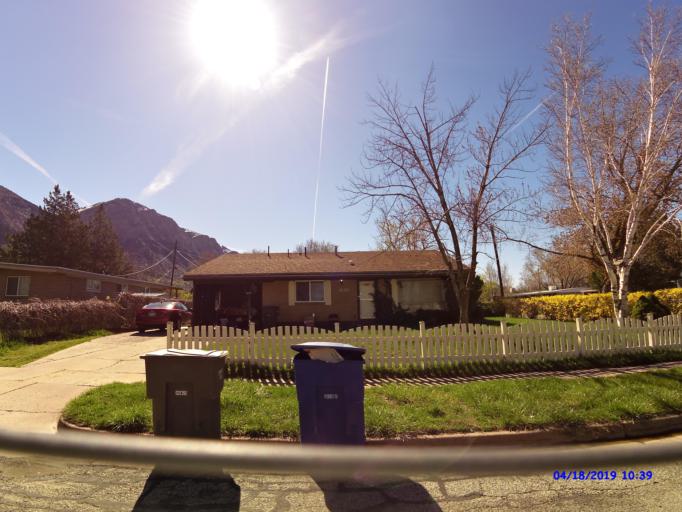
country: US
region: Utah
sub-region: Weber County
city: Harrisville
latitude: 41.2722
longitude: -111.9626
